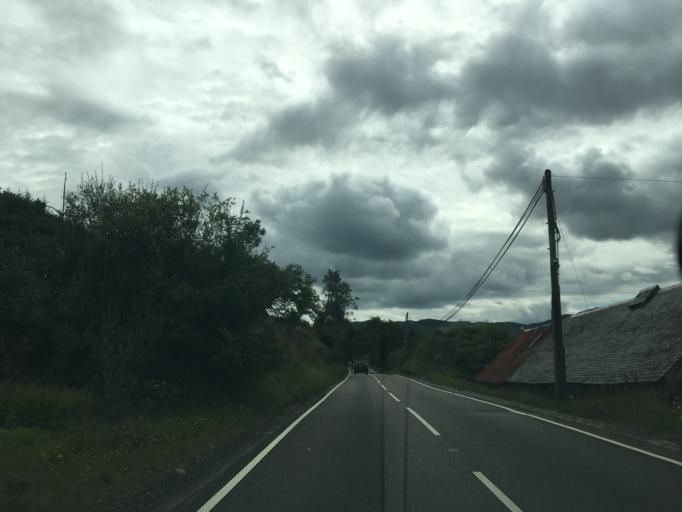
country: GB
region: Scotland
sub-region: Stirling
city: Callander
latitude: 56.3444
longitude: -4.3270
